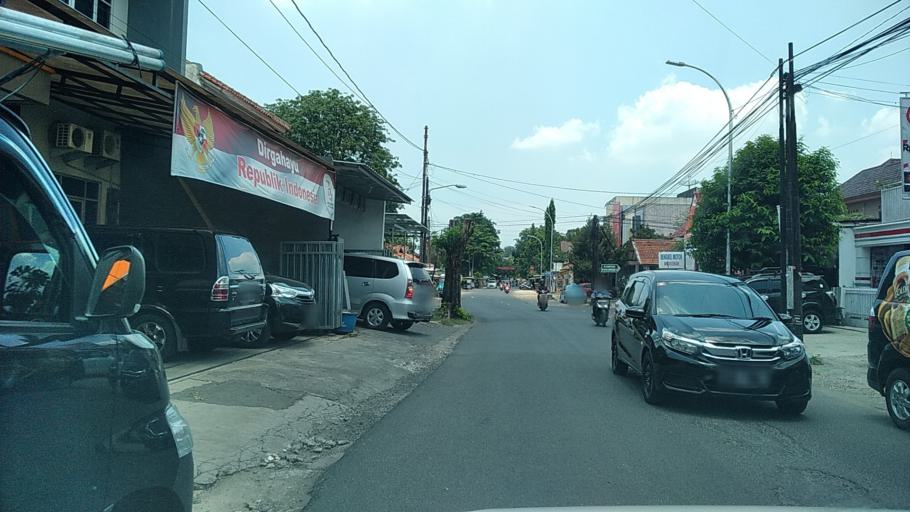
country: ID
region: Central Java
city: Semarang
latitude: -7.0134
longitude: 110.3949
